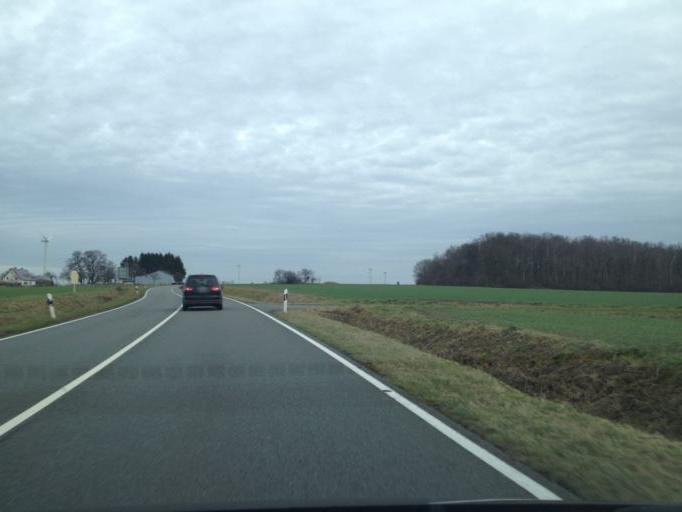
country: DE
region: North Rhine-Westphalia
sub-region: Regierungsbezirk Arnsberg
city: Mohnesee
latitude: 51.5057
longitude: 8.0668
